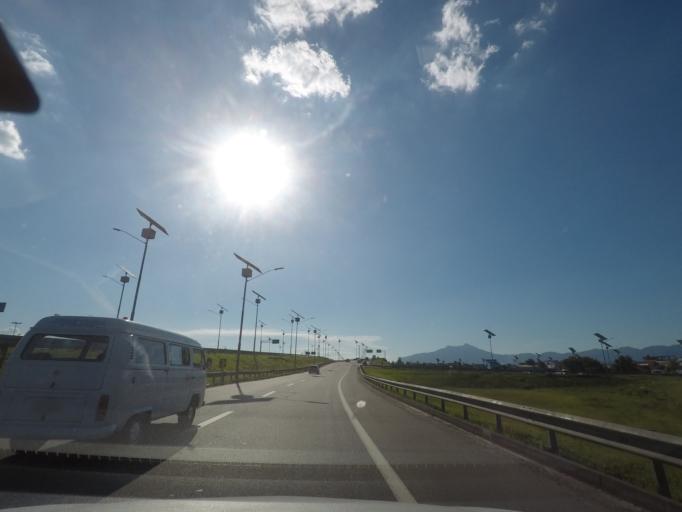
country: BR
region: Rio de Janeiro
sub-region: Duque De Caxias
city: Duque de Caxias
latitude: -22.6720
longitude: -43.2823
